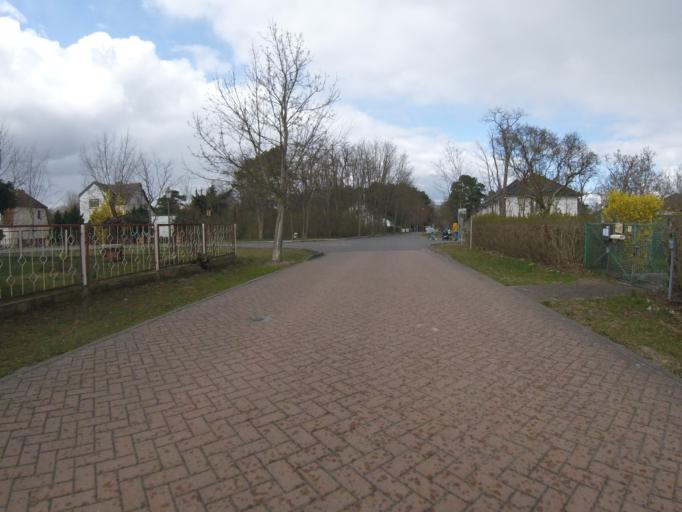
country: DE
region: Brandenburg
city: Bestensee
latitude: 52.2252
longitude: 13.6611
